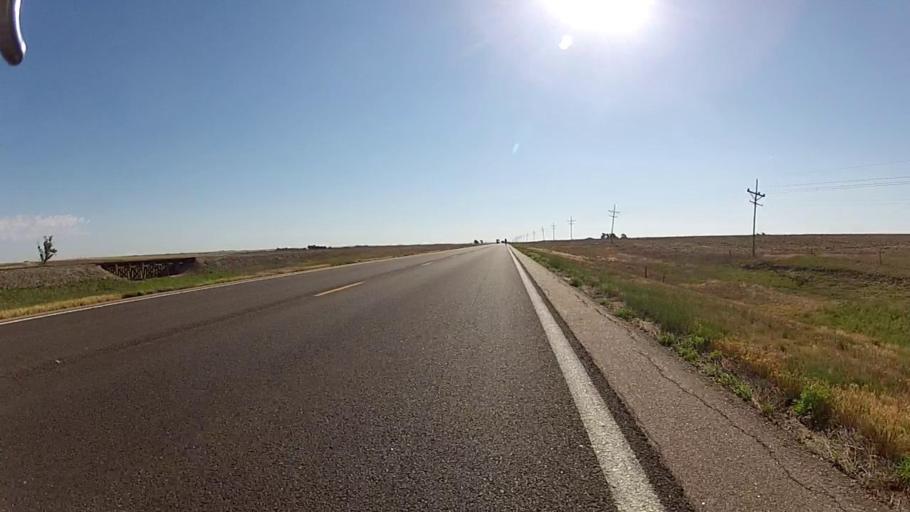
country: US
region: Kansas
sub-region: Haskell County
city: Sublette
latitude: 37.5488
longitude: -100.6074
